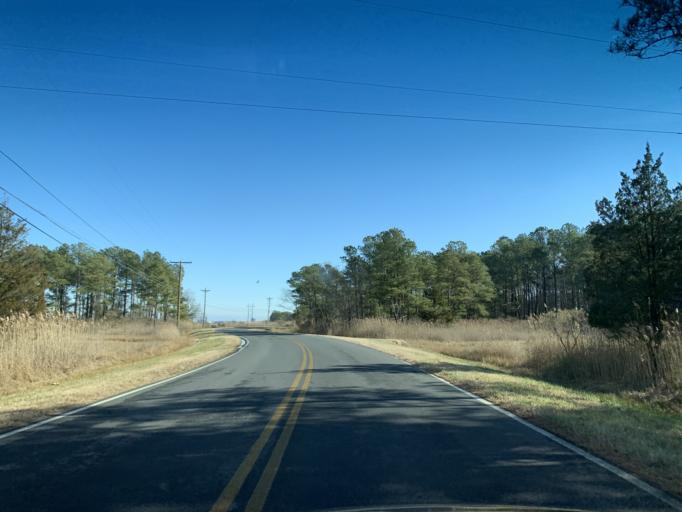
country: US
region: Maryland
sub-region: Worcester County
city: Ocean Pines
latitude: 38.4146
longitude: -75.1185
